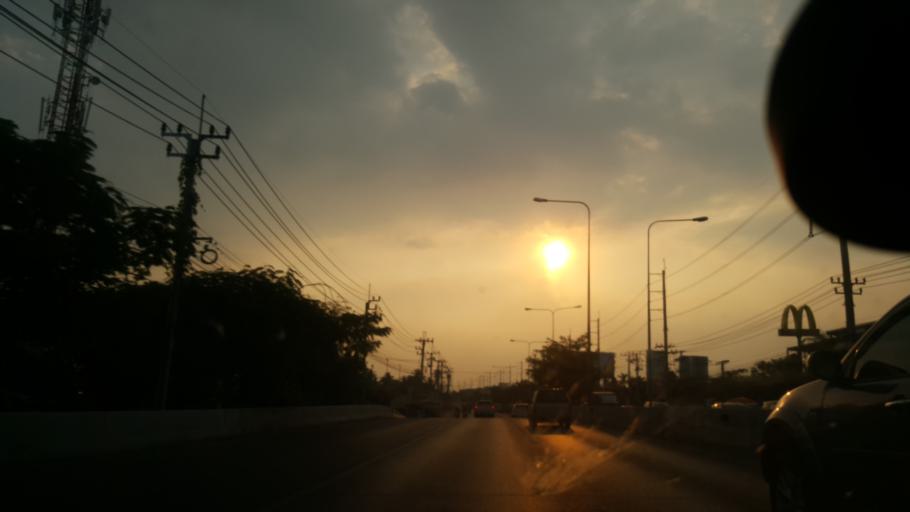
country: TH
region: Bangkok
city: Phasi Charoen
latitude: 13.7088
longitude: 100.4521
